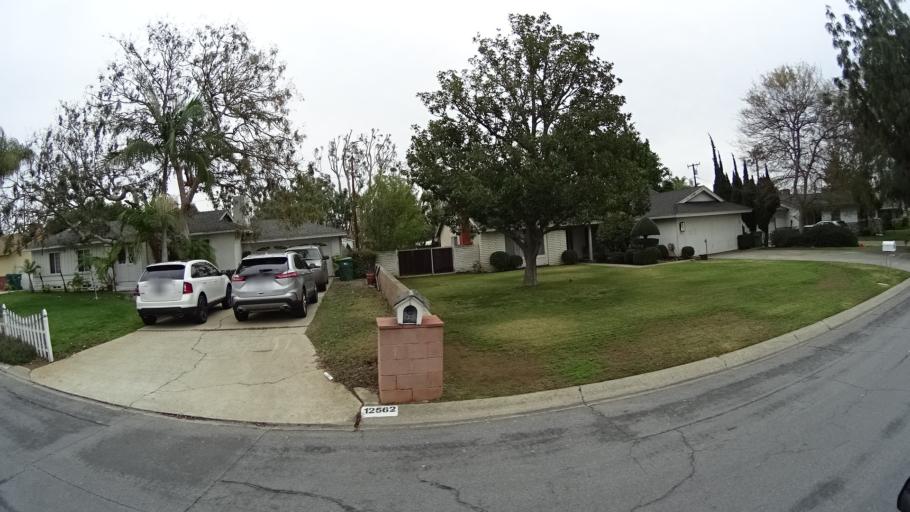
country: US
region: California
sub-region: Orange County
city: North Tustin
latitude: 33.7503
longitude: -117.8008
